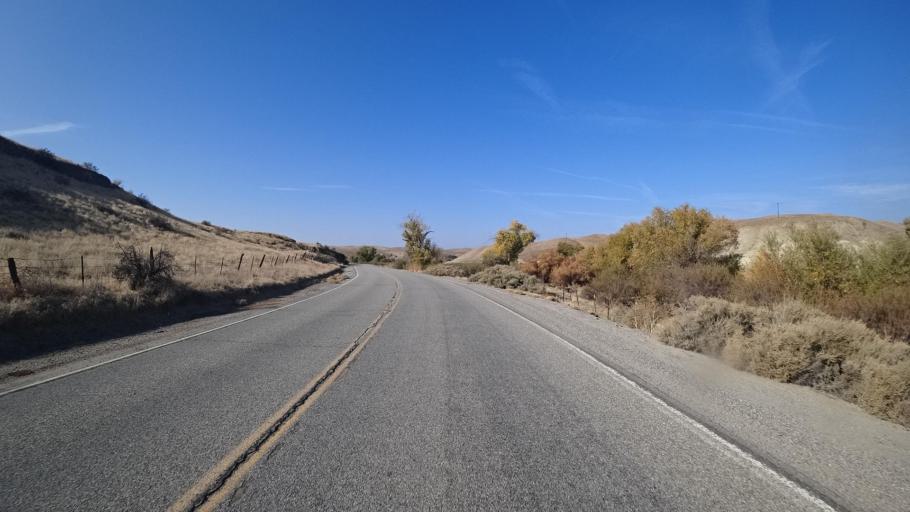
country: US
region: California
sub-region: Kern County
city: Oildale
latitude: 35.5293
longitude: -118.9648
